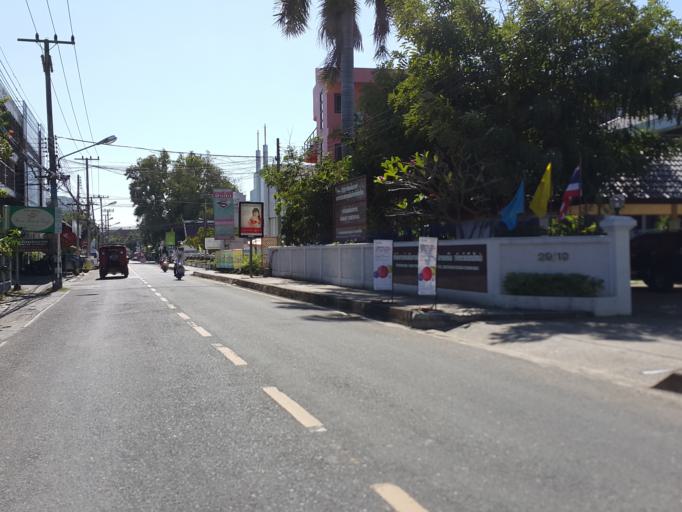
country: TH
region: Chiang Mai
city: Chiang Mai
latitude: 18.7941
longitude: 98.9819
